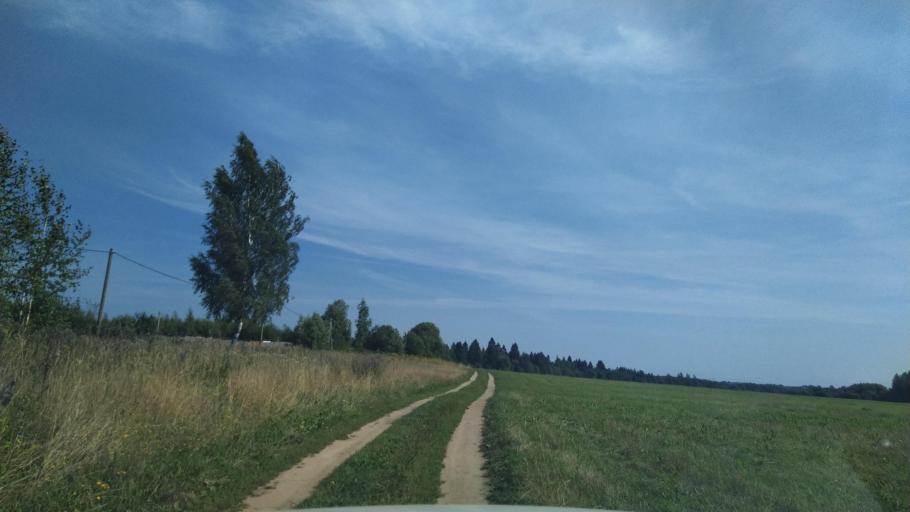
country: RU
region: Leningrad
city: Druzhnaya Gorka
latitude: 59.2681
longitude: 30.0554
